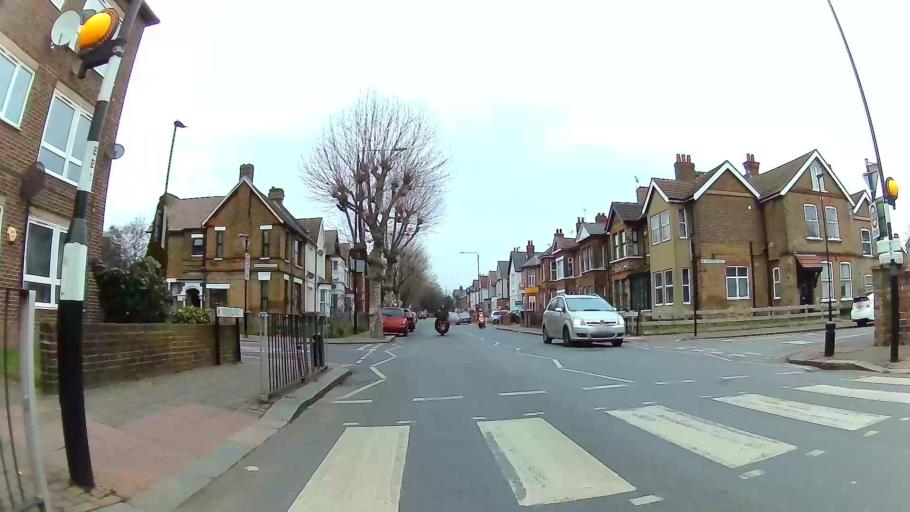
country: GB
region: England
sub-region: Greater London
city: East Ham
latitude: 51.5354
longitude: 0.0223
